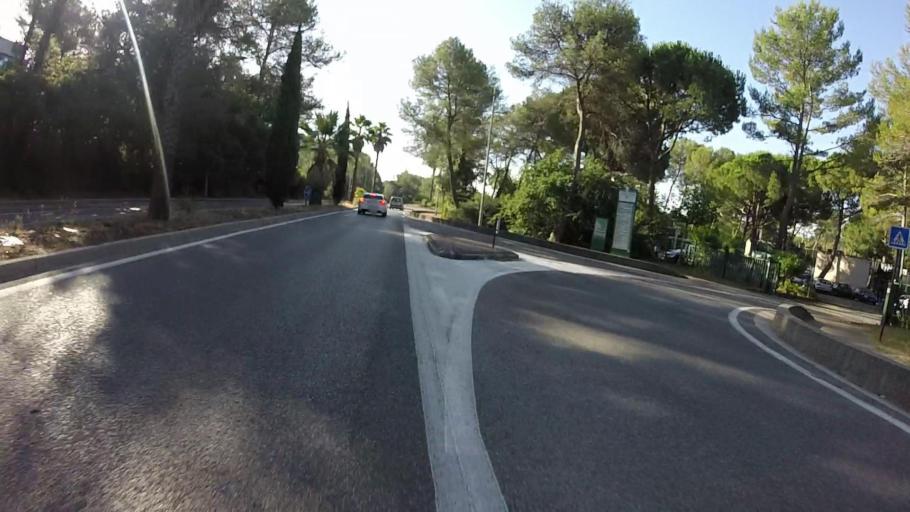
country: FR
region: Provence-Alpes-Cote d'Azur
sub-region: Departement des Alpes-Maritimes
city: Mougins
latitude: 43.6118
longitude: 7.0164
